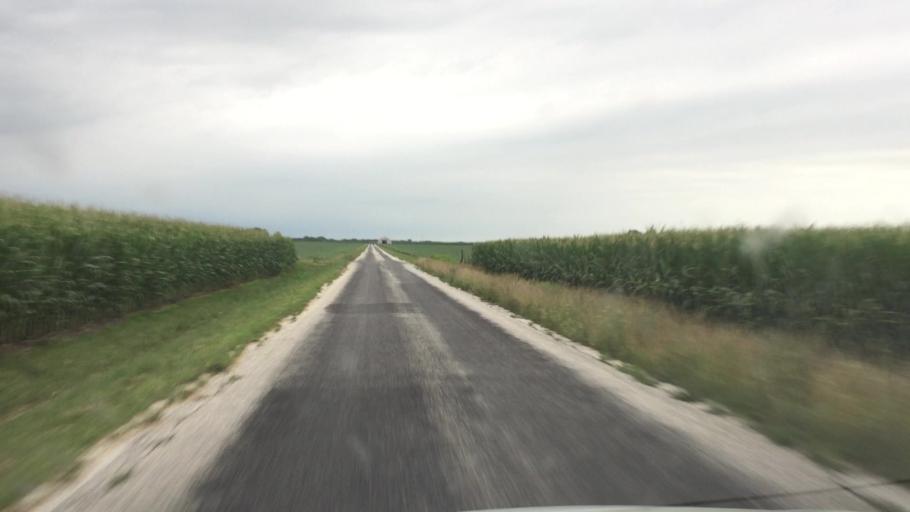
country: US
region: Illinois
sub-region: Adams County
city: Camp Point
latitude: 40.2223
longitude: -90.9691
